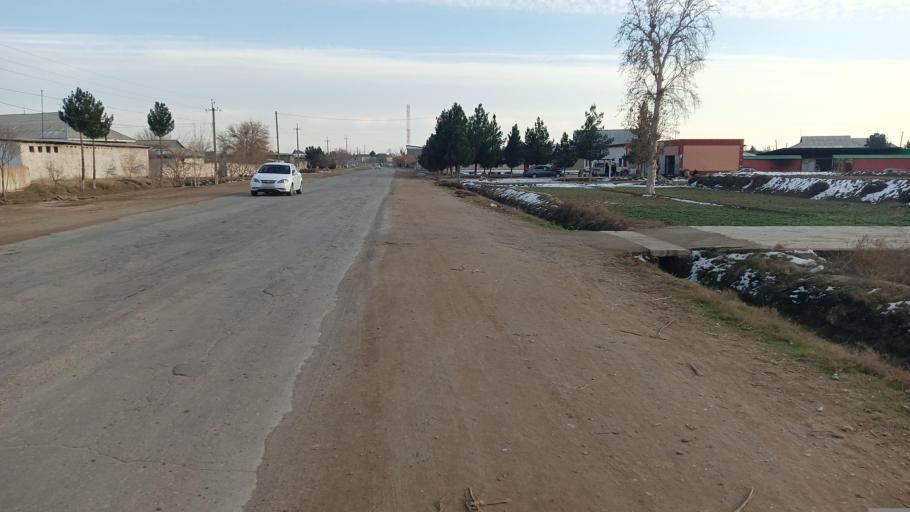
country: UZ
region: Qashqadaryo
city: Yangi Mirishkor
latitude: 38.8931
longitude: 65.3036
